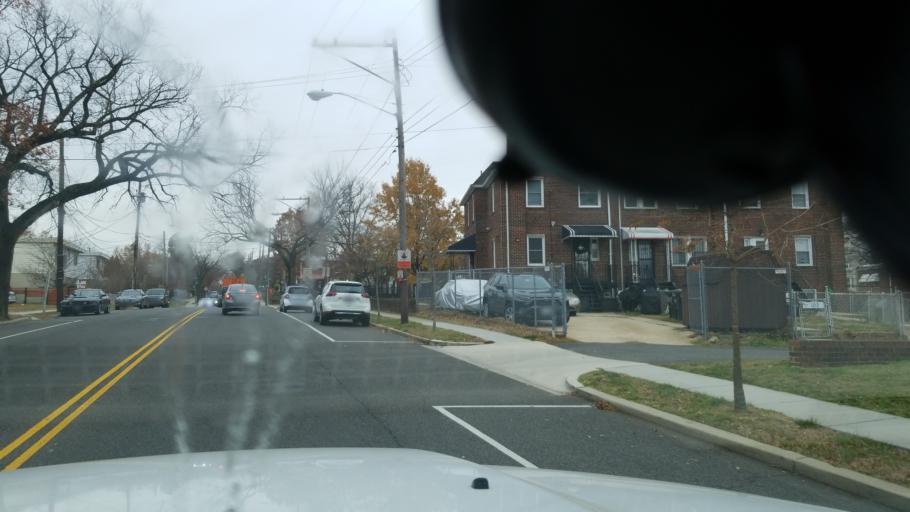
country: US
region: Maryland
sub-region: Prince George's County
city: Chillum
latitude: 38.9476
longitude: -76.9893
